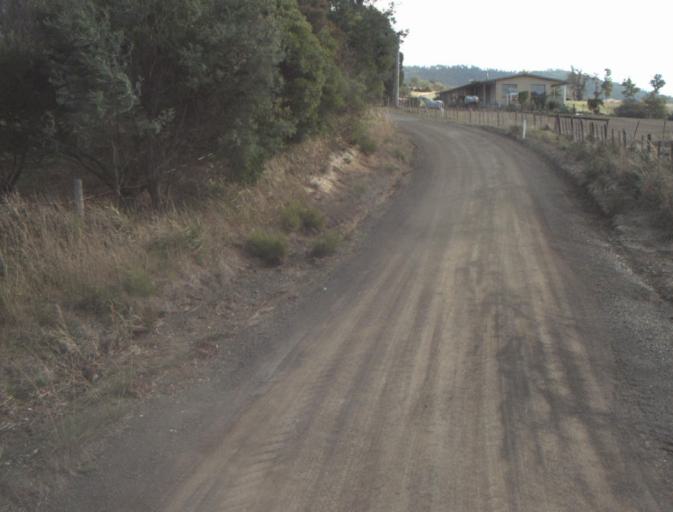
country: AU
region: Tasmania
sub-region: Launceston
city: Mayfield
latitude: -41.2139
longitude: 147.1422
